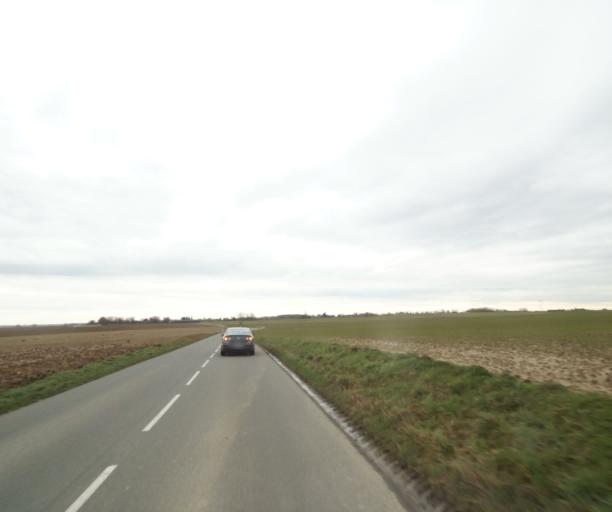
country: FR
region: Nord-Pas-de-Calais
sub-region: Departement du Nord
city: Sebourg
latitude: 50.3528
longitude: 3.6212
